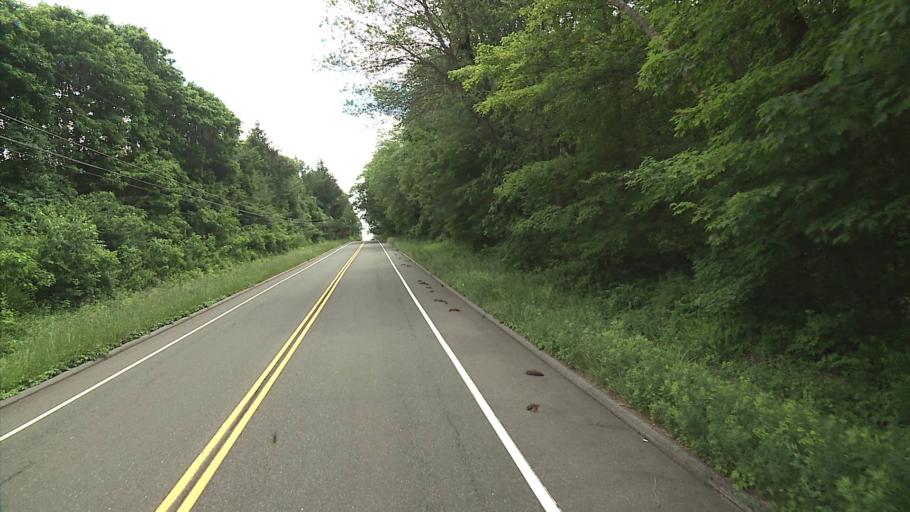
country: US
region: Connecticut
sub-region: Litchfield County
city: Bethlehem Village
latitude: 41.6594
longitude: -73.1552
